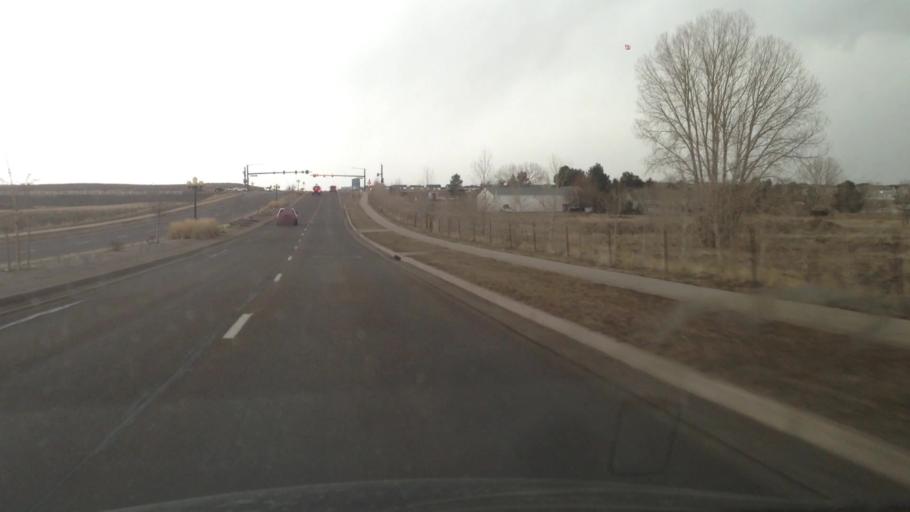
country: US
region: Colorado
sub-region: Douglas County
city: Parker
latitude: 39.4932
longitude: -104.7706
